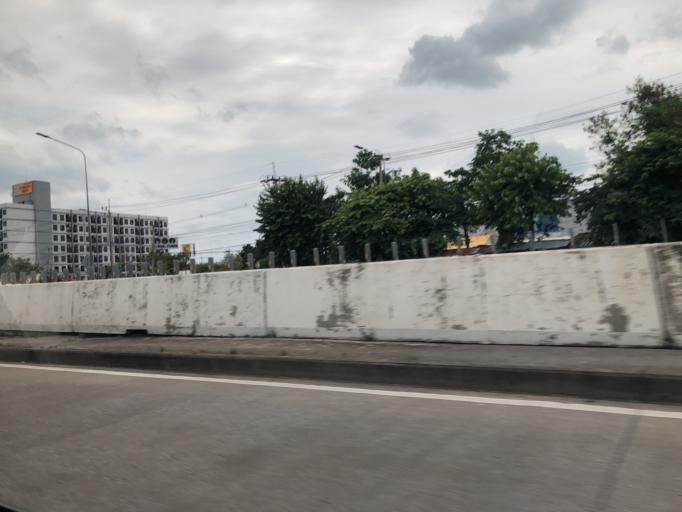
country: TH
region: Nonthaburi
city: Pak Kret
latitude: 13.9089
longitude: 100.5173
